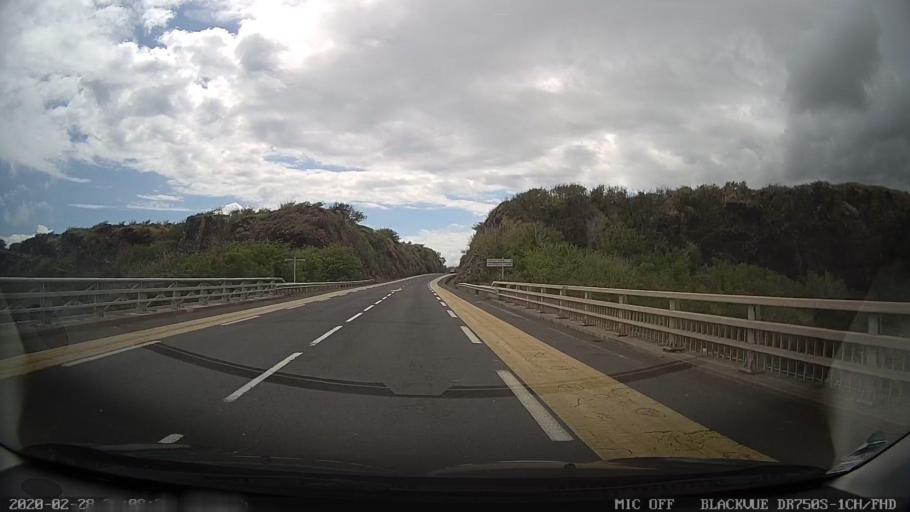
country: RE
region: Reunion
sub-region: Reunion
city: Trois-Bassins
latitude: -21.1258
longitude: 55.2676
